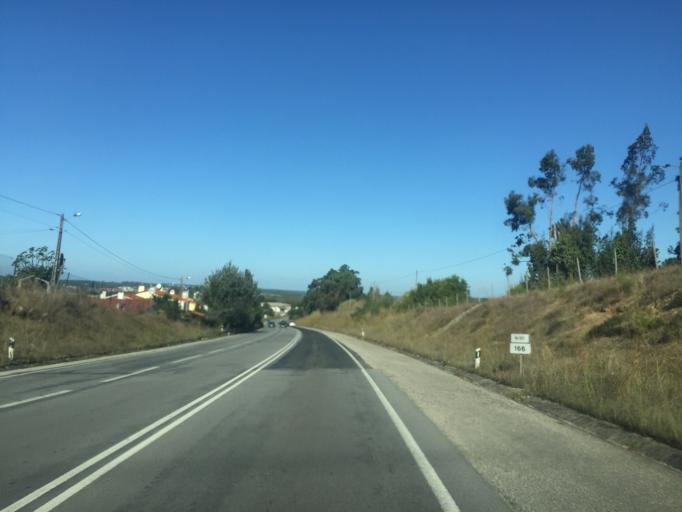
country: PT
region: Leiria
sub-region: Leiria
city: Leiria
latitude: 39.7737
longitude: -8.8174
